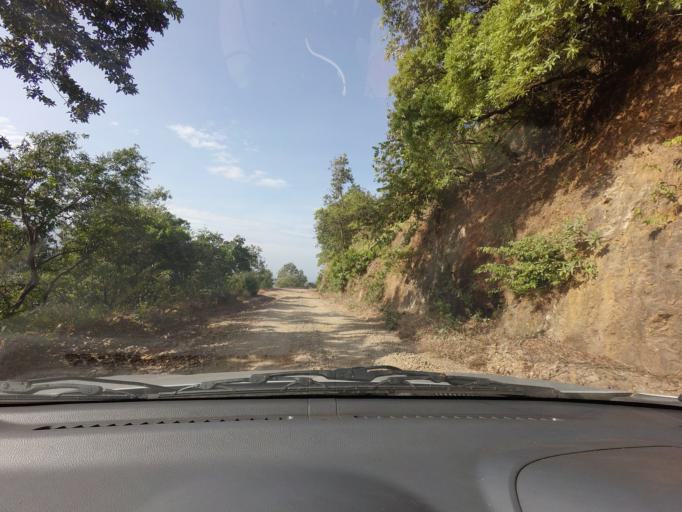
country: IN
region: Karnataka
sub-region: Kodagu
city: Somvarpet
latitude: 12.7100
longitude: 75.6747
